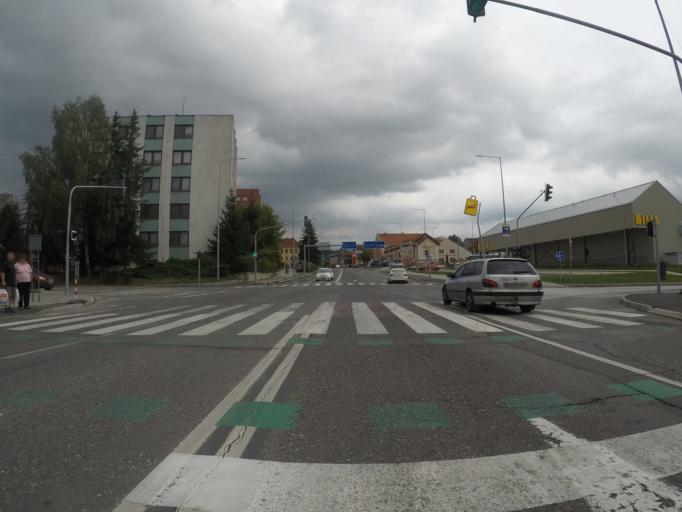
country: SK
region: Kosicky
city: Spisska Nova Ves
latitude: 48.9436
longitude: 20.5617
